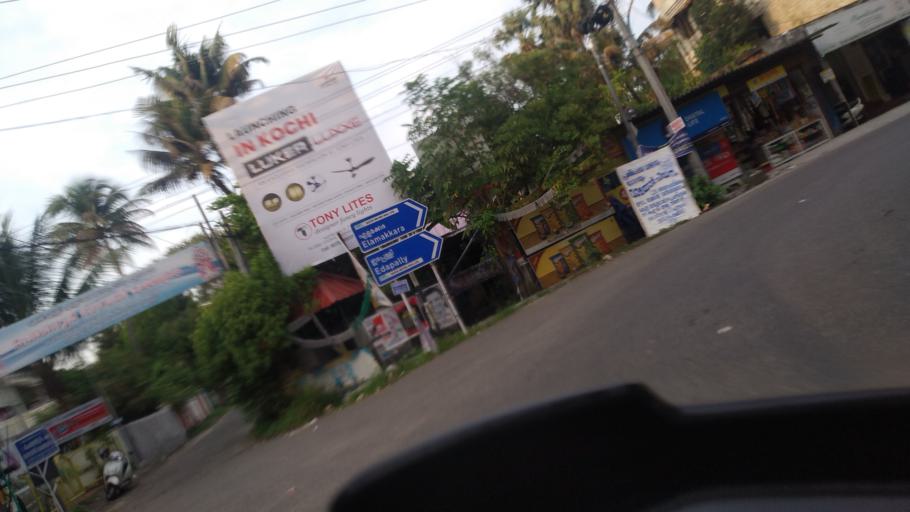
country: IN
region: Kerala
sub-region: Ernakulam
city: Elur
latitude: 10.0180
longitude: 76.2843
